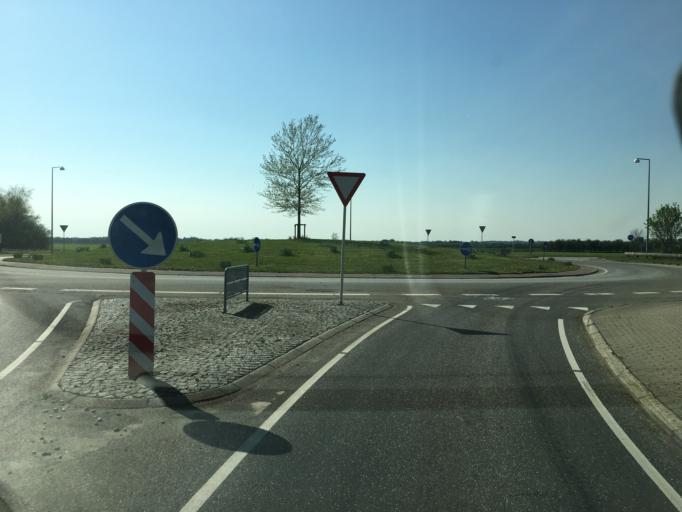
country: DK
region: South Denmark
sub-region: Haderslev Kommune
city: Vojens
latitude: 55.3105
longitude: 9.2820
